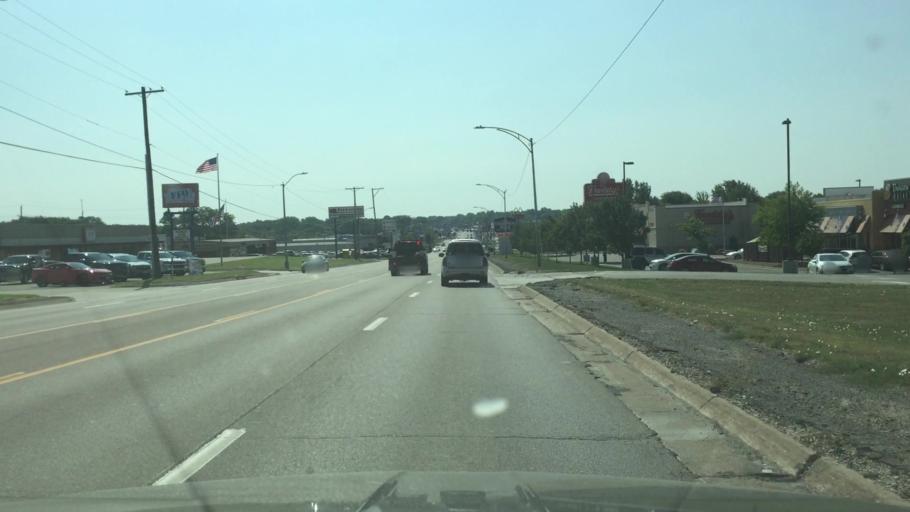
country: US
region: Missouri
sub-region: Pettis County
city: Sedalia
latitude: 38.7099
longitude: -93.2691
